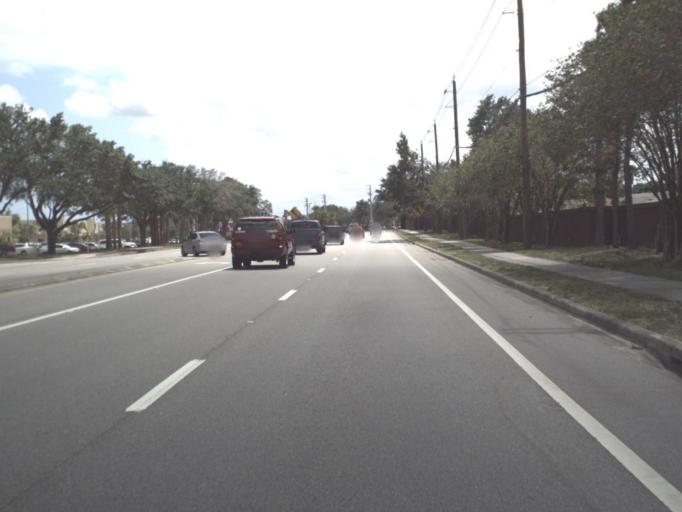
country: US
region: Florida
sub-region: Brevard County
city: South Patrick Shores
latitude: 28.2212
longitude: -80.6764
